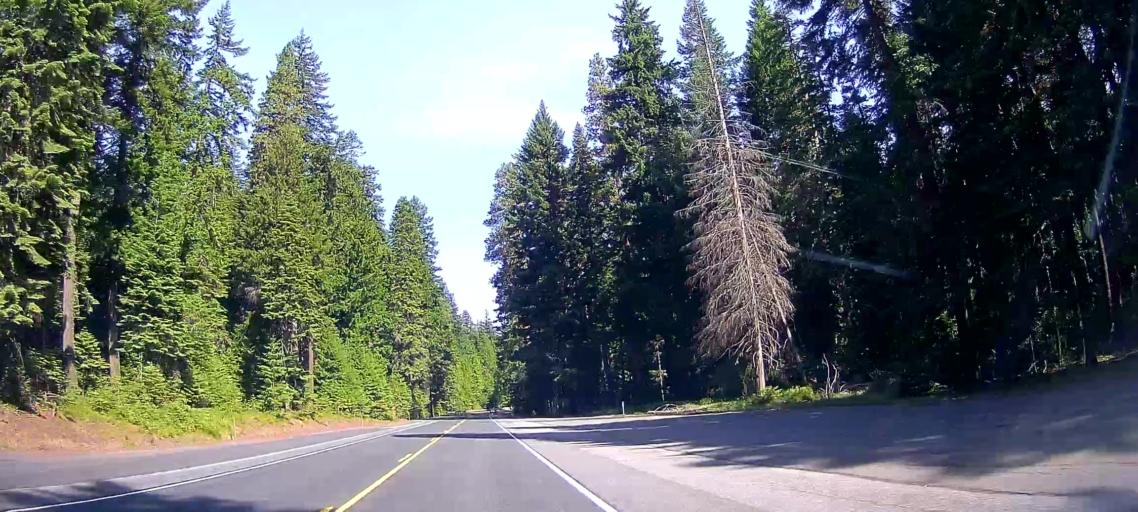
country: US
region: Oregon
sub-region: Jefferson County
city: Warm Springs
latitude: 45.0926
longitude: -121.5506
